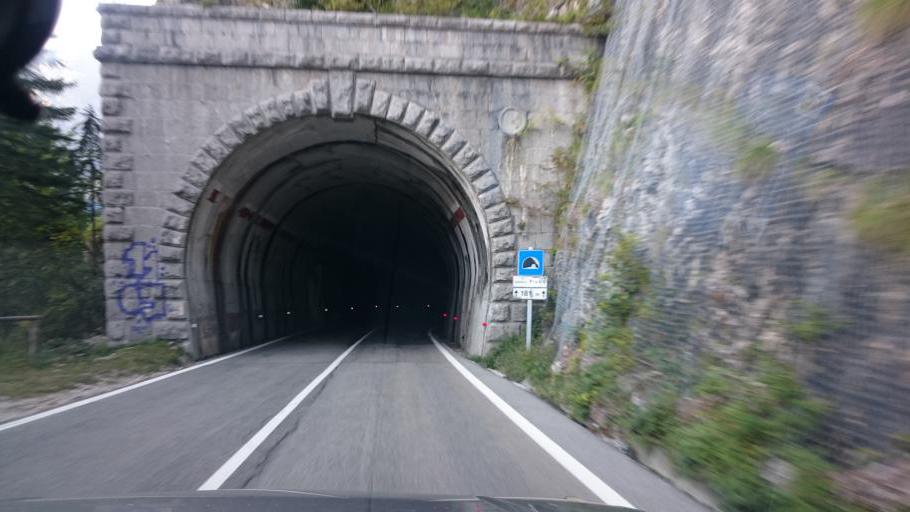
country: IT
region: Friuli Venezia Giulia
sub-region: Provincia di Udine
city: Tarvisio
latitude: 46.4230
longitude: 13.5704
